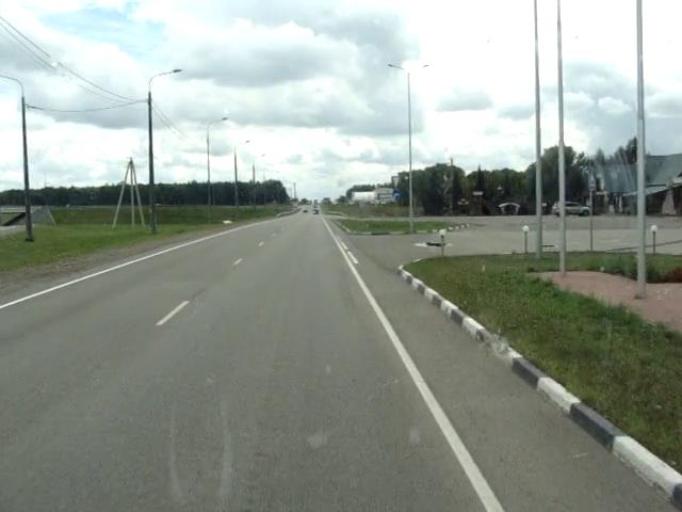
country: RU
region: Altai Krai
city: Zarya
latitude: 52.5797
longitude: 85.1765
